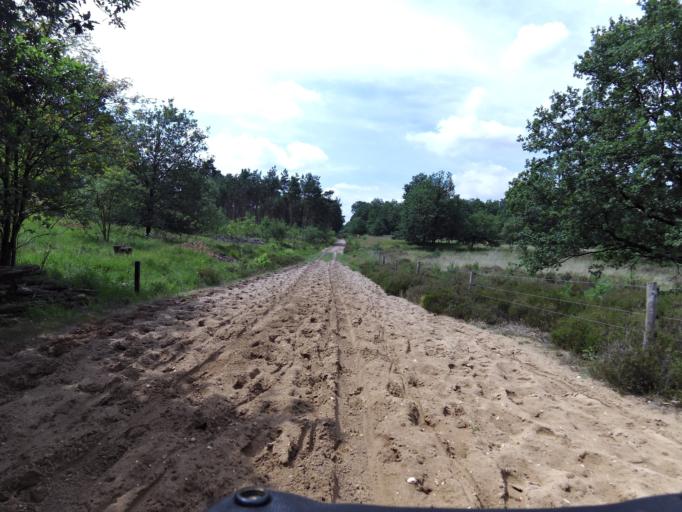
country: NL
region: Limburg
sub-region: Gemeente Roerdalen
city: Vlodrop
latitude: 51.1725
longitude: 6.1334
